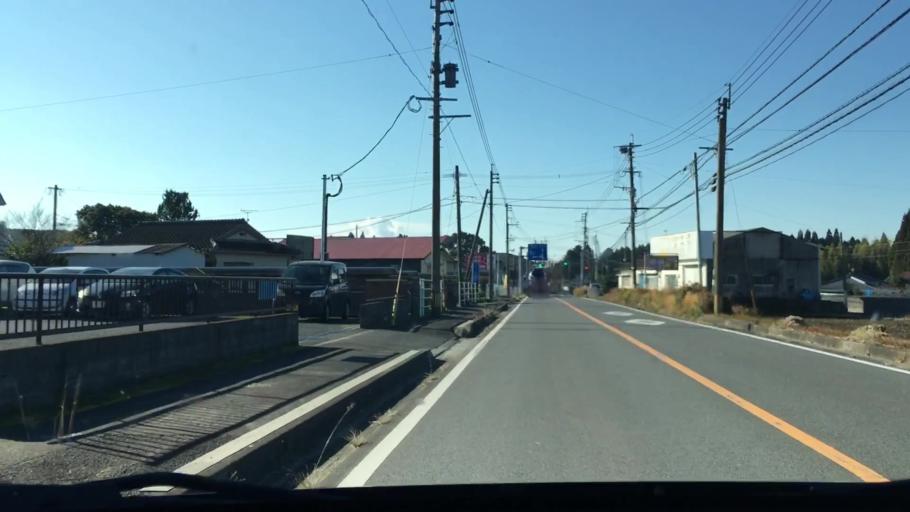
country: JP
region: Kagoshima
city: Kajiki
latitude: 31.7797
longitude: 130.7035
